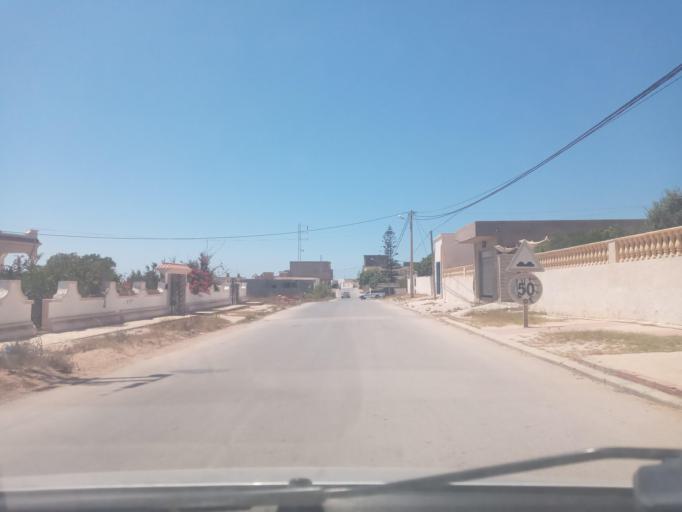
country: TN
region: Nabul
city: El Haouaria
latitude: 37.0535
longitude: 10.9948
